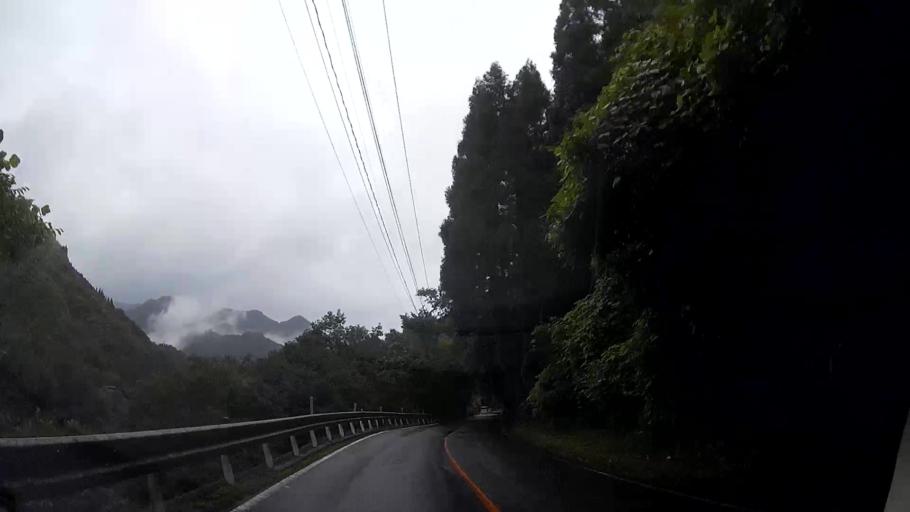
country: JP
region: Oita
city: Hita
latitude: 33.1792
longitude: 131.0063
